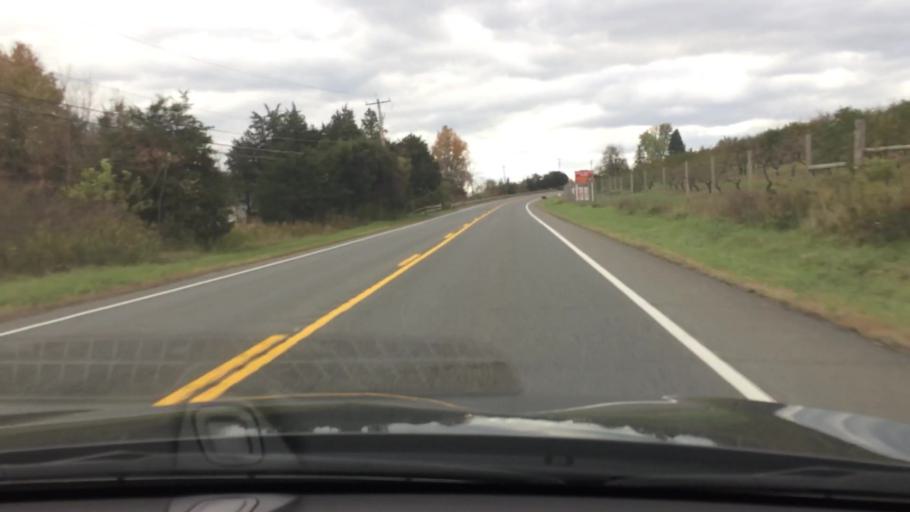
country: US
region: New York
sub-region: Columbia County
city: Stottville
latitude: 42.3153
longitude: -73.7016
